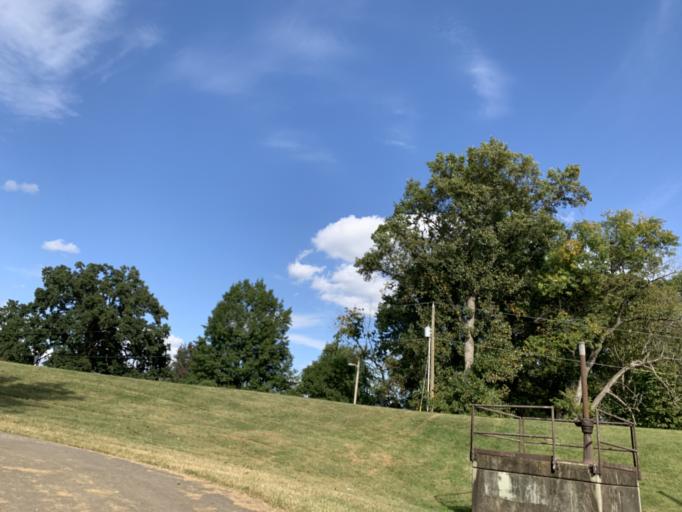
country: US
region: Indiana
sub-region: Floyd County
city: New Albany
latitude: 38.2507
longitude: -85.8317
